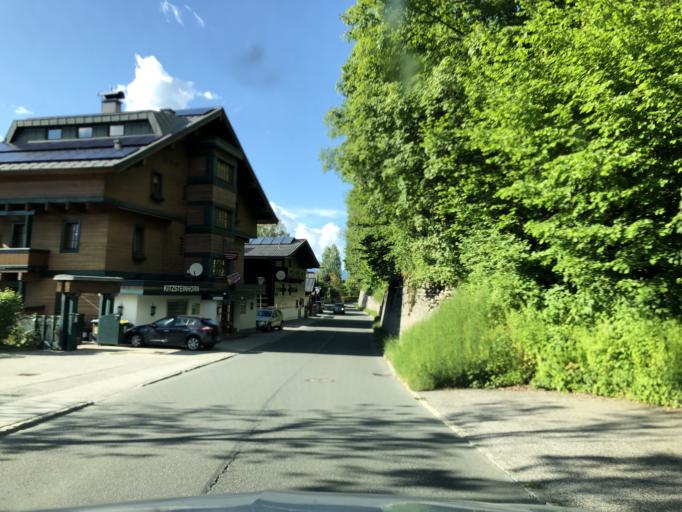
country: AT
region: Salzburg
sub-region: Politischer Bezirk Zell am See
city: Zell am See
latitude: 47.3150
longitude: 12.8153
